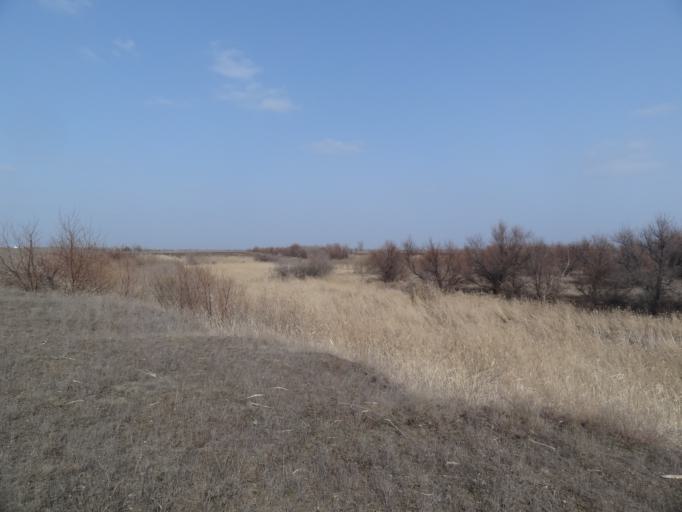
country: RU
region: Saratov
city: Shumeyka
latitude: 51.4566
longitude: 46.2781
